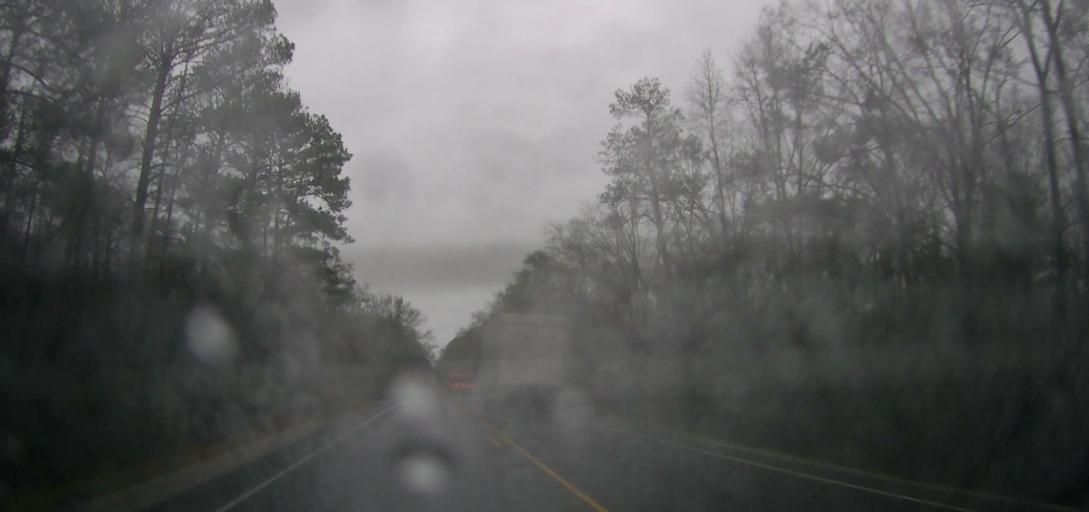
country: US
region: Alabama
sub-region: Autauga County
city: Pine Level
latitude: 32.5696
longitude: -86.6774
